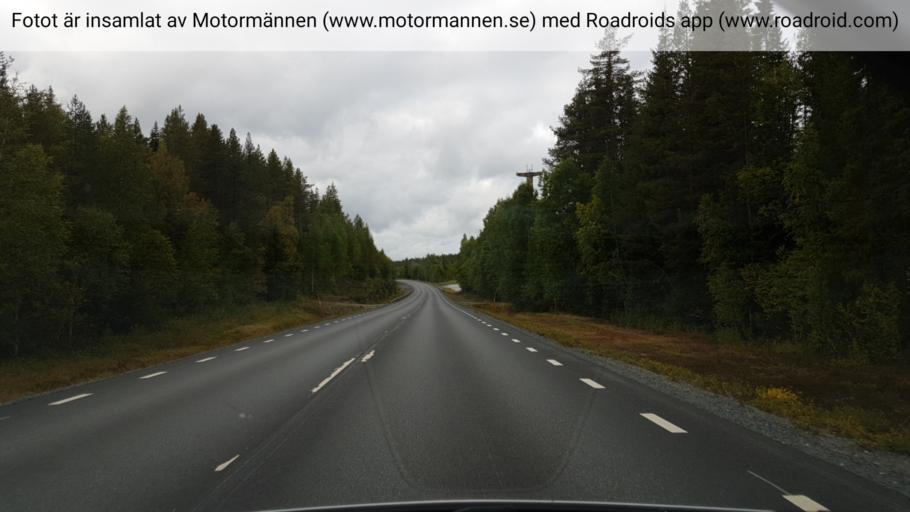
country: SE
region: Vaesterbotten
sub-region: Norsjo Kommun
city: Norsjoe
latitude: 64.9717
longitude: 19.7497
